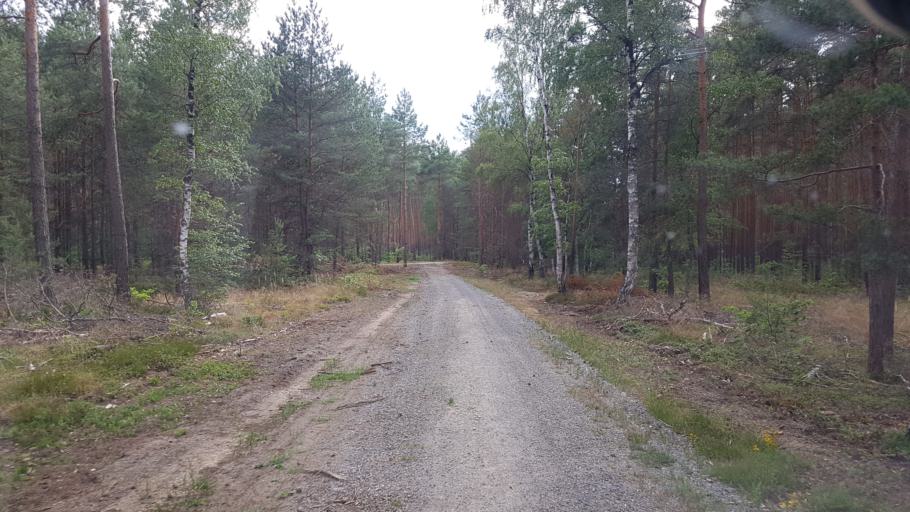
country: DE
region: Brandenburg
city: Schonborn
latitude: 51.5647
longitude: 13.4636
